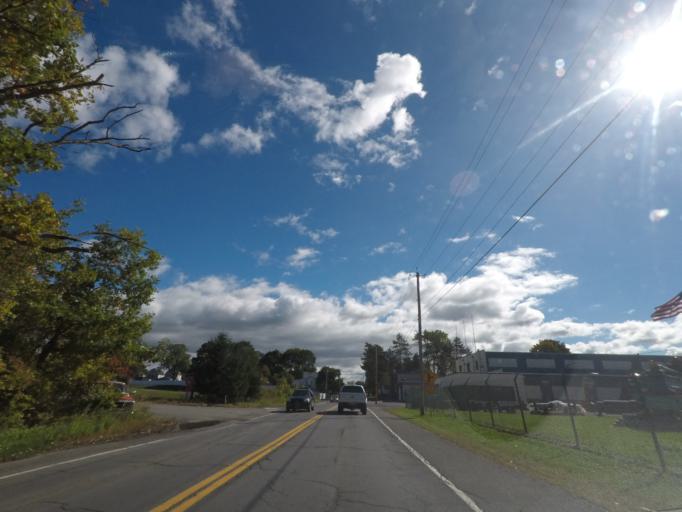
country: US
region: New York
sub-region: Albany County
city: Menands
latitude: 42.7096
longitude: -73.7170
